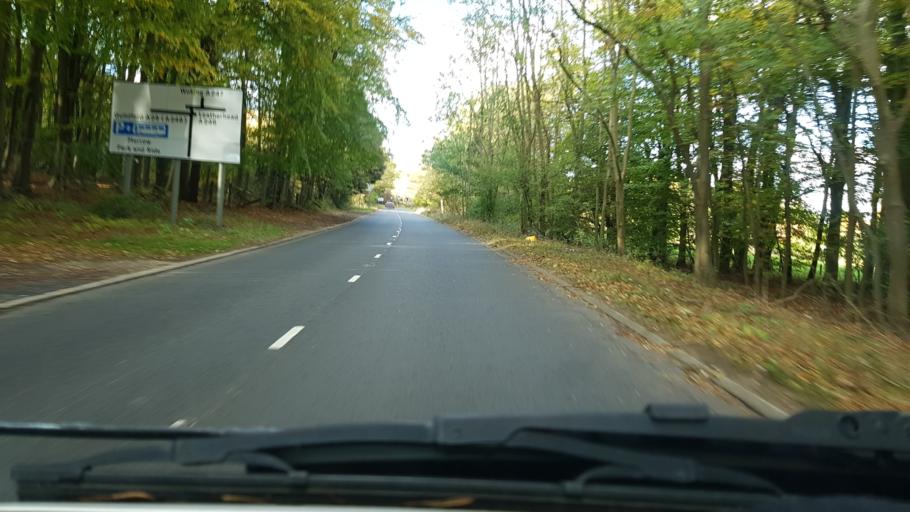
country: GB
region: England
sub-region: Surrey
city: Chilworth
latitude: 51.2465
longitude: -0.5021
